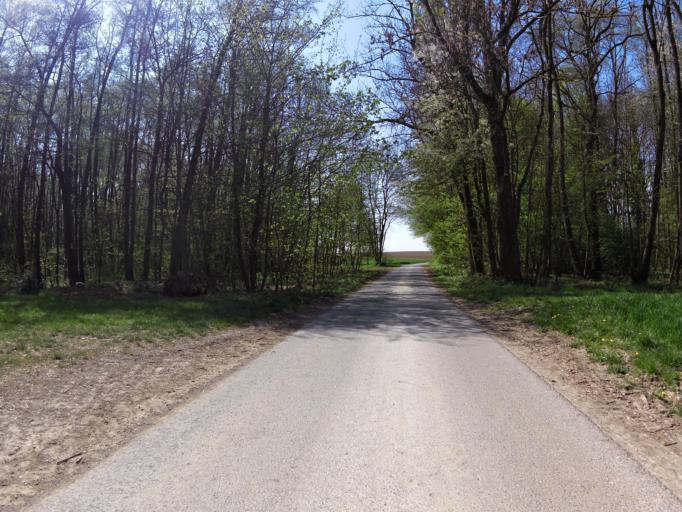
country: DE
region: Bavaria
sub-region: Regierungsbezirk Unterfranken
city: Eibelstadt
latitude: 49.6956
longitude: 9.9636
